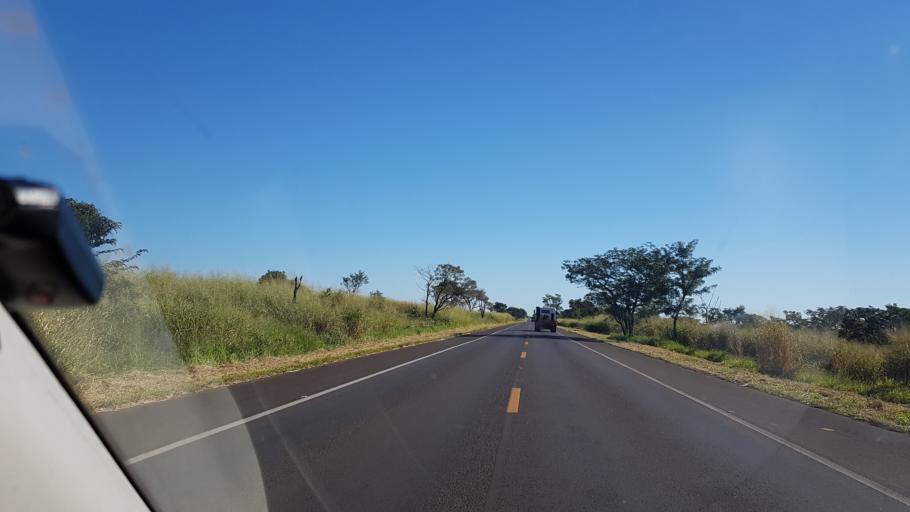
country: BR
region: Sao Paulo
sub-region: Maracai
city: Maracai
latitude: -22.5564
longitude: -50.5284
